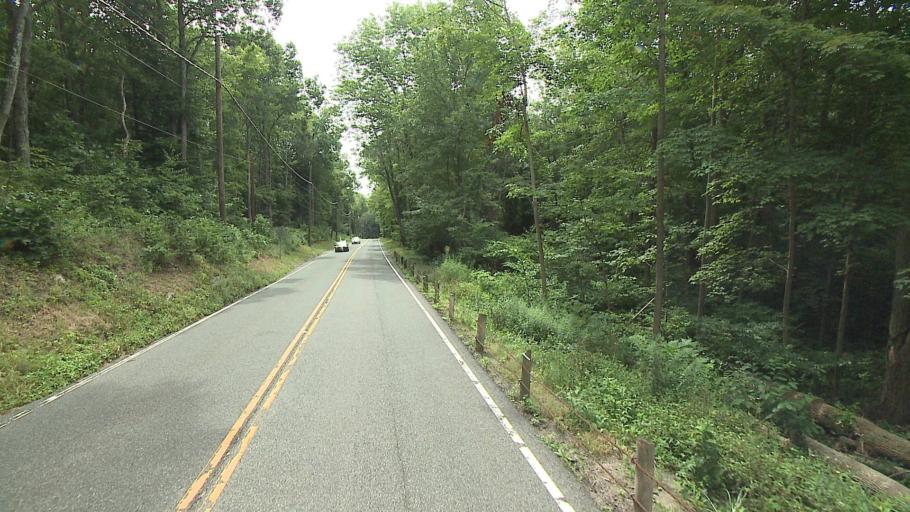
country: US
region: Connecticut
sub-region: Litchfield County
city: Bethlehem Village
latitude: 41.6052
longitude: -73.2848
